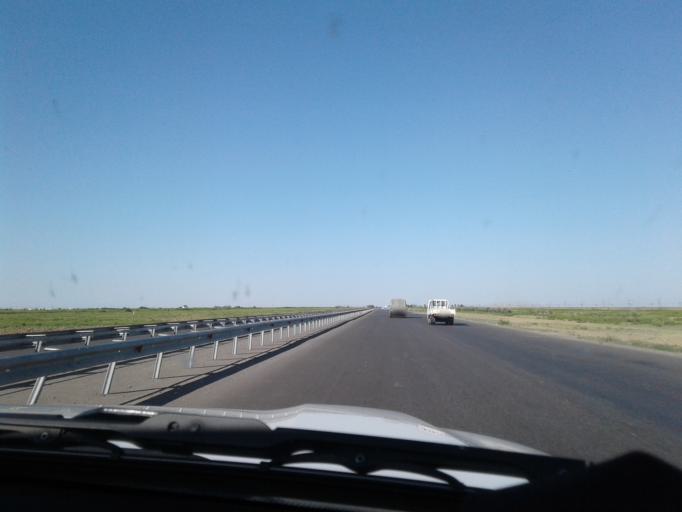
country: TM
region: Ahal
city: Tejen
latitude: 37.3029
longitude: 60.3097
